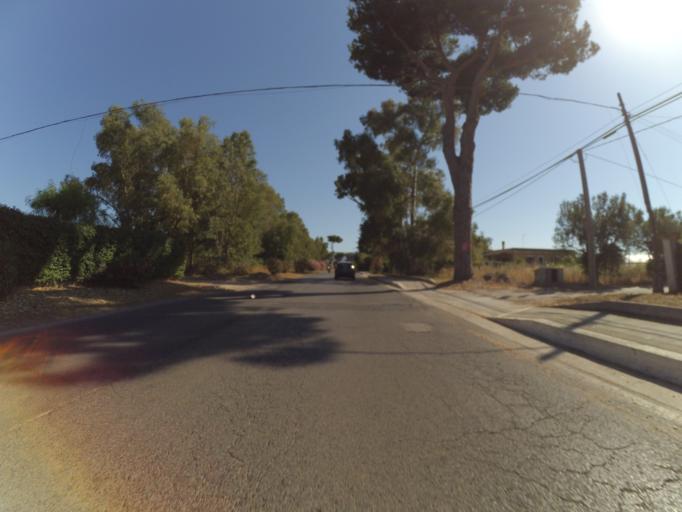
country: IT
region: Latium
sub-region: Provincia di Latina
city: San Felice Circeo
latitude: 41.2824
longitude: 13.1041
